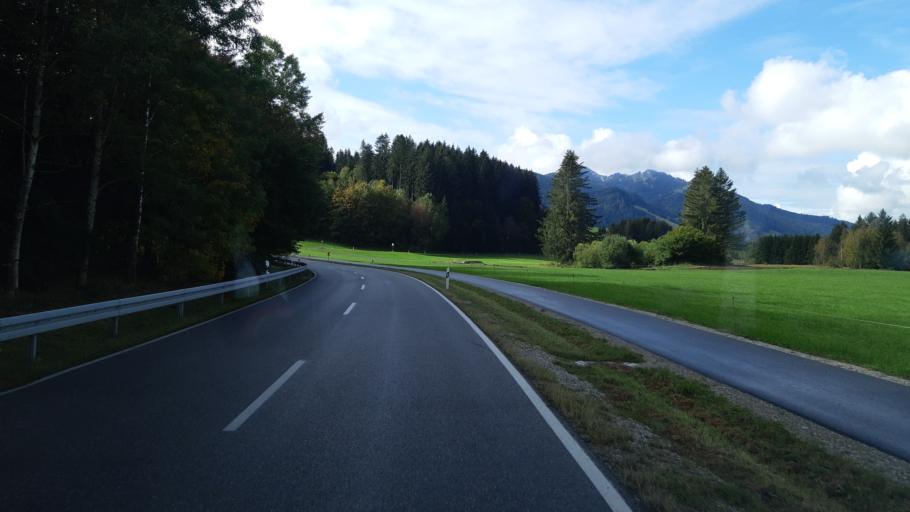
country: DE
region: Bavaria
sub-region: Swabia
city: Eisenberg
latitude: 47.6023
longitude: 10.5833
